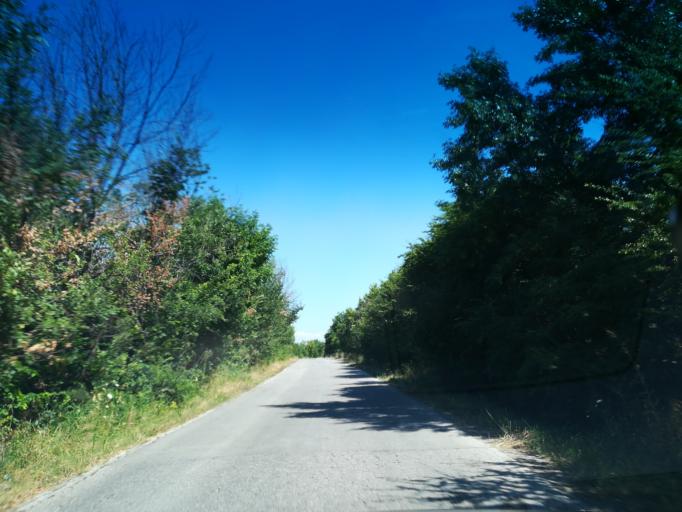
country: BG
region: Plovdiv
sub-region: Obshtina Sadovo
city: Sadovo
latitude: 42.0160
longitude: 25.0366
